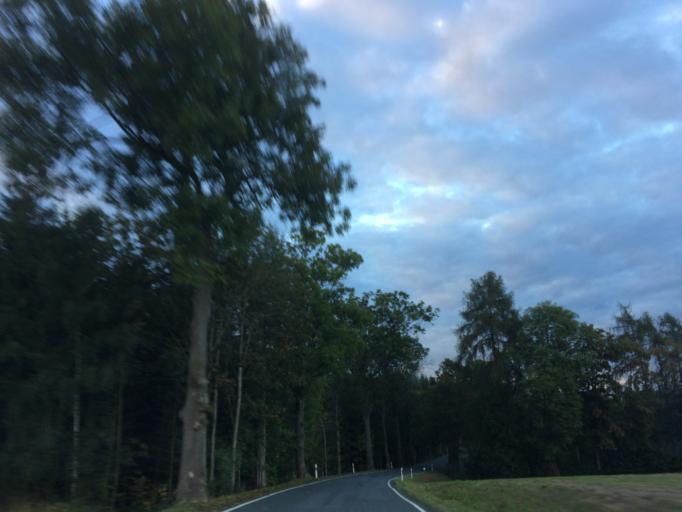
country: DE
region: Thuringia
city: Paska
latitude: 50.6299
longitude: 11.6435
